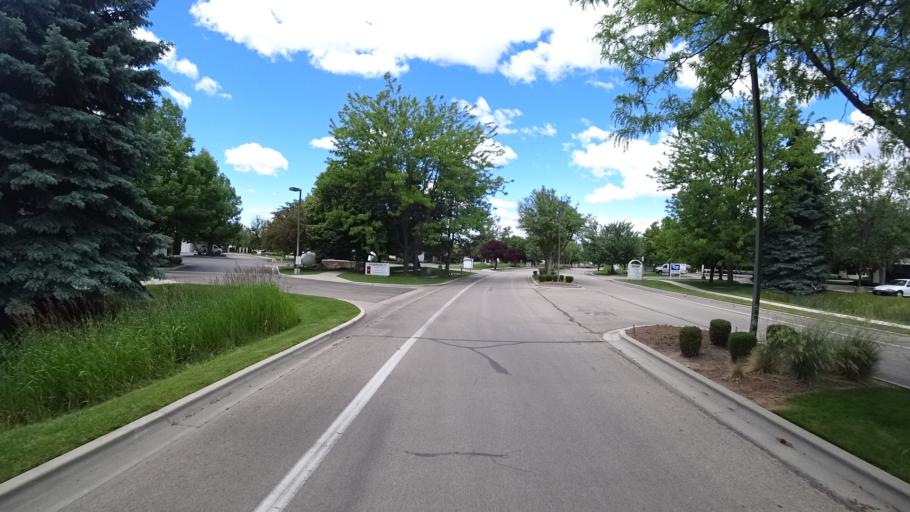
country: US
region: Idaho
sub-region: Ada County
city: Eagle
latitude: 43.6599
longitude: -116.3377
